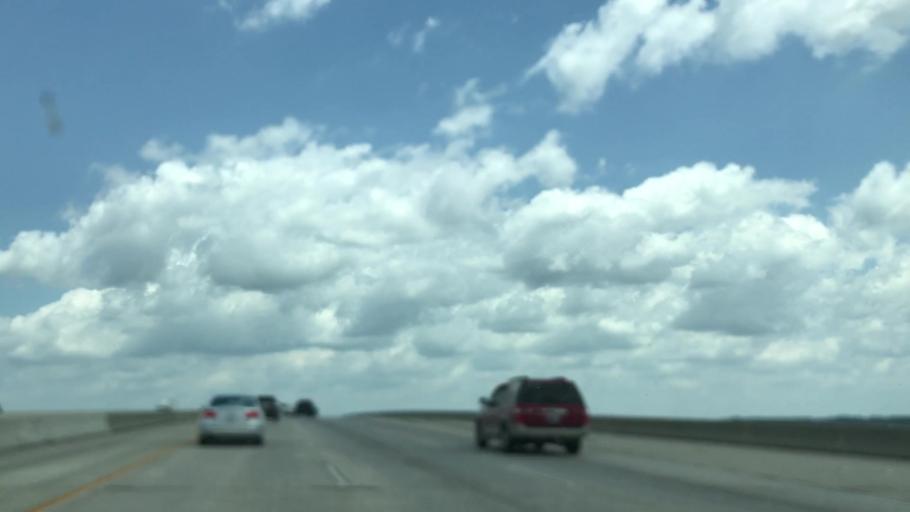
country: US
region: Georgia
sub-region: Glynn County
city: Dock Junction
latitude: 31.1896
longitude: -81.5412
